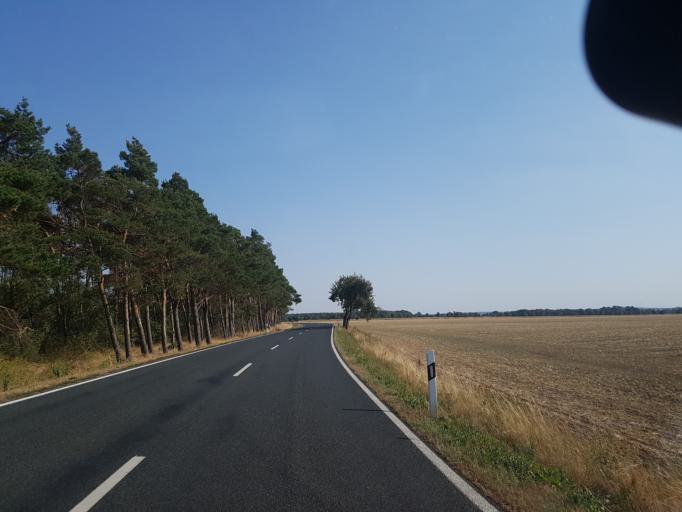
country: DE
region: Saxony
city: Beilrode
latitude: 51.5567
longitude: 13.0805
